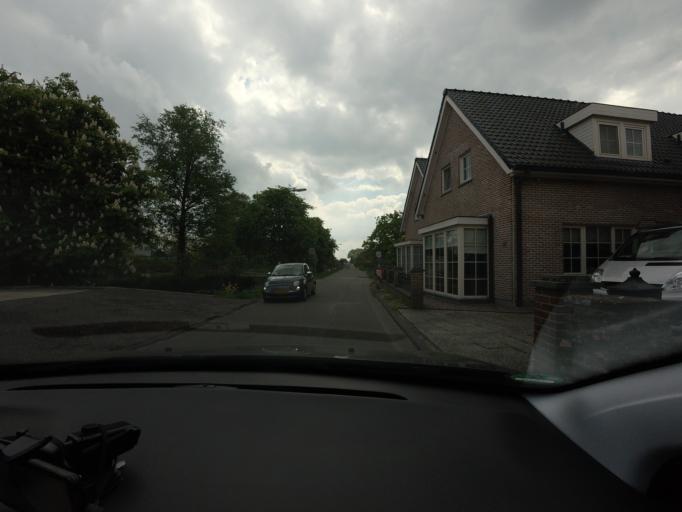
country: NL
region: Utrecht
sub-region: Gemeente De Ronde Venen
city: Mijdrecht
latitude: 52.2110
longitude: 4.9356
